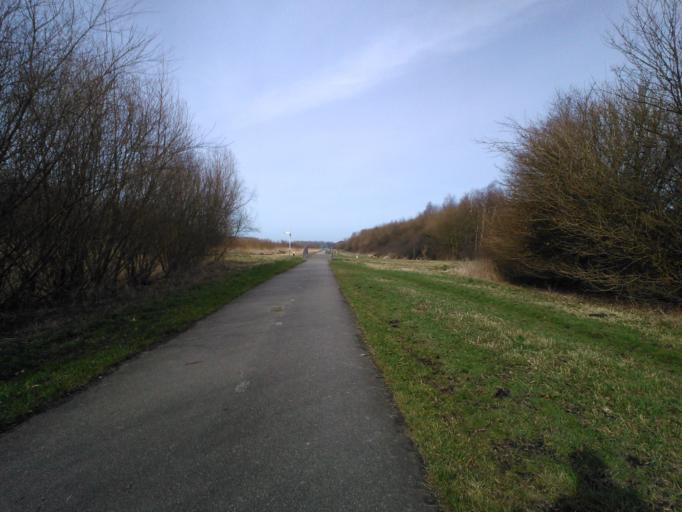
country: NL
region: South Holland
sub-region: Gemeente Pijnacker-Nootdorp
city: Pijnacker
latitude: 52.0368
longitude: 4.4470
